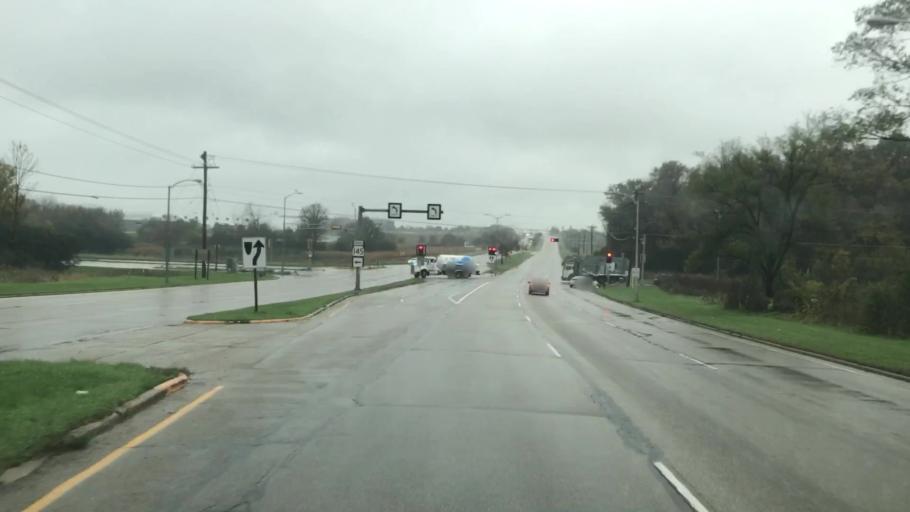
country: US
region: Wisconsin
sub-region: Waukesha County
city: Menomonee Falls
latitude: 43.1768
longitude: -88.0621
